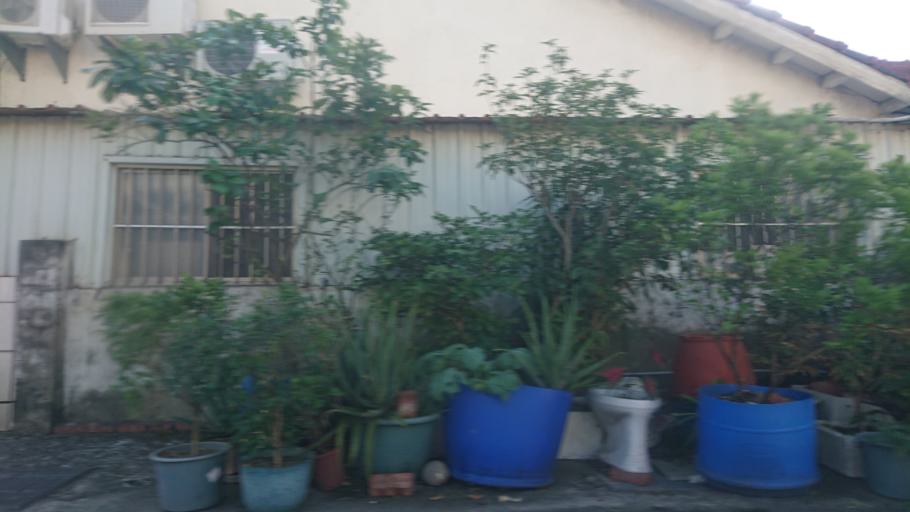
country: TW
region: Taiwan
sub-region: Tainan
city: Tainan
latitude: 23.0131
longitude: 120.2337
